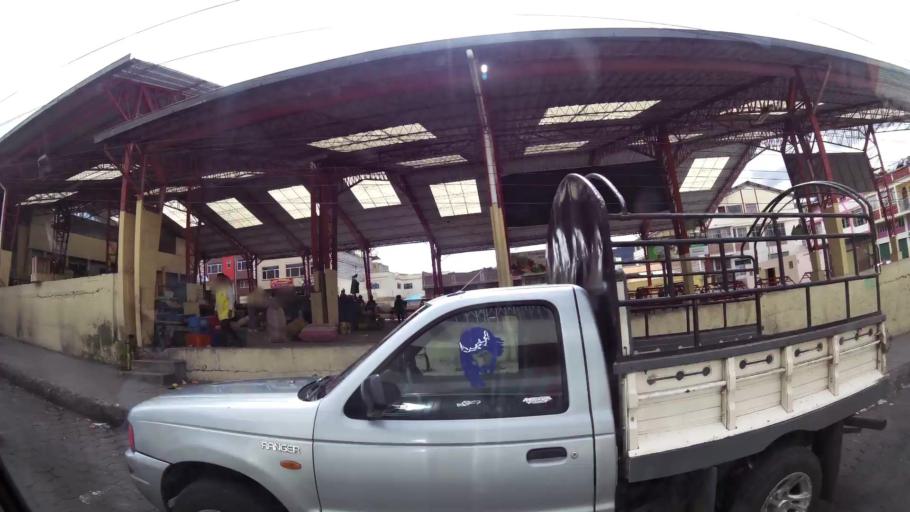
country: EC
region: Tungurahua
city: Ambato
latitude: -1.2477
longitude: -78.6245
